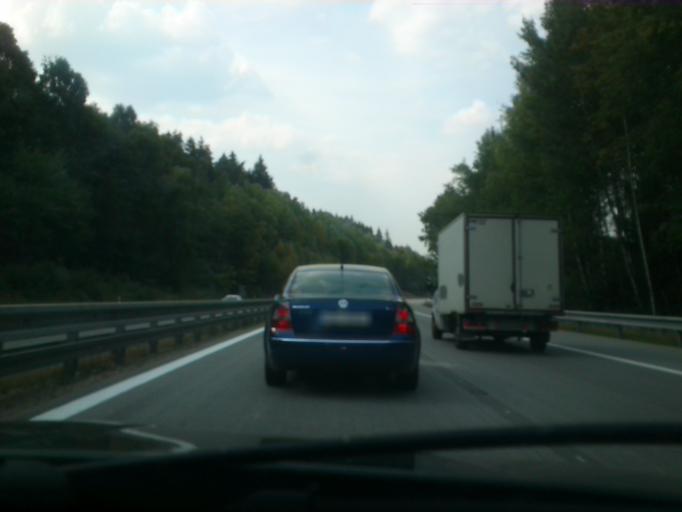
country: CZ
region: Central Bohemia
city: Vlasim
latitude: 49.7617
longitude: 14.9535
